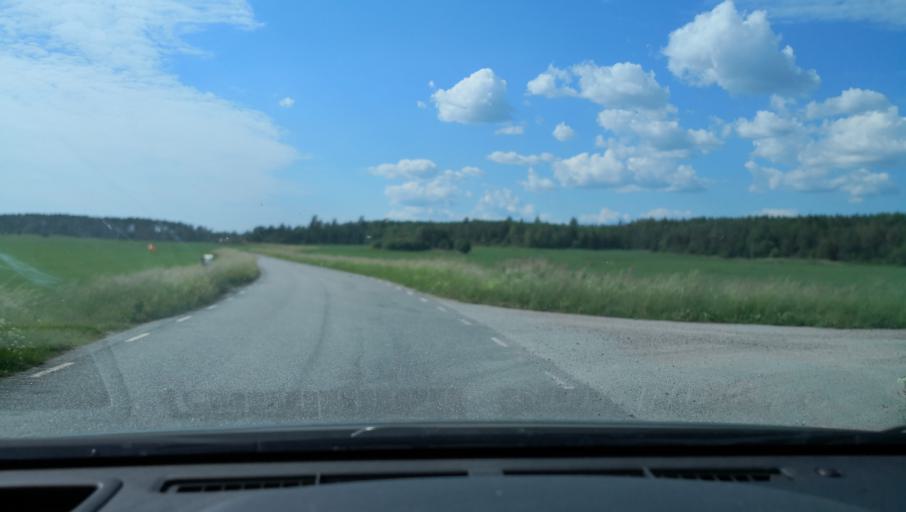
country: SE
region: Uppsala
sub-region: Enkopings Kommun
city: Orsundsbro
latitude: 59.8367
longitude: 17.3022
